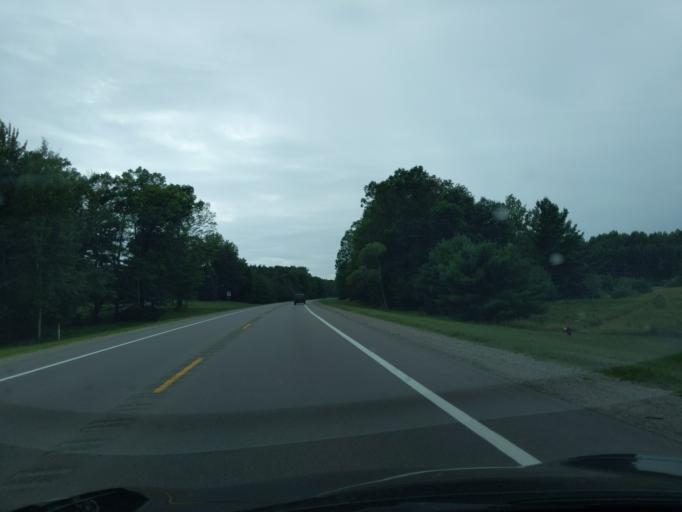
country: US
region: Michigan
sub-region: Clare County
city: Harrison
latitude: 44.0186
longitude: -84.8155
